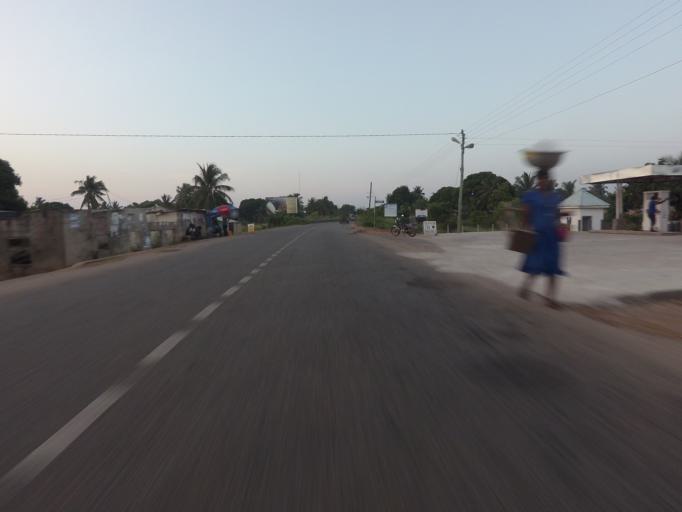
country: GH
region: Volta
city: Keta
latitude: 5.8759
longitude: 0.9806
